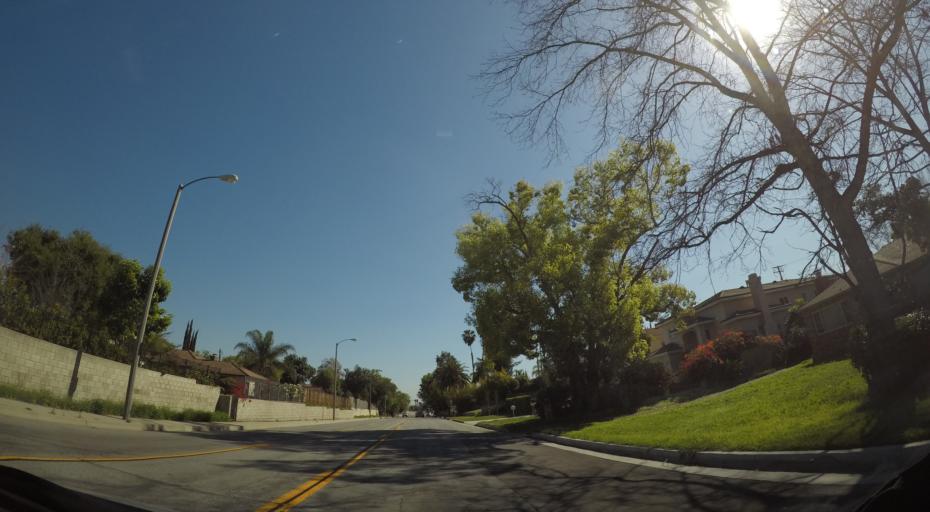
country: US
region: California
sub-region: Los Angeles County
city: East Pasadena
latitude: 34.1363
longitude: -118.0676
